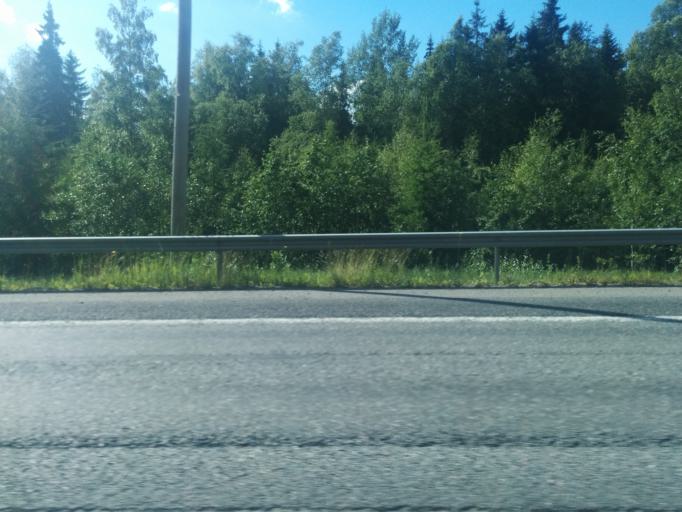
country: FI
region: Pirkanmaa
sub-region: Tampere
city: Tampere
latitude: 61.5171
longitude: 23.9174
